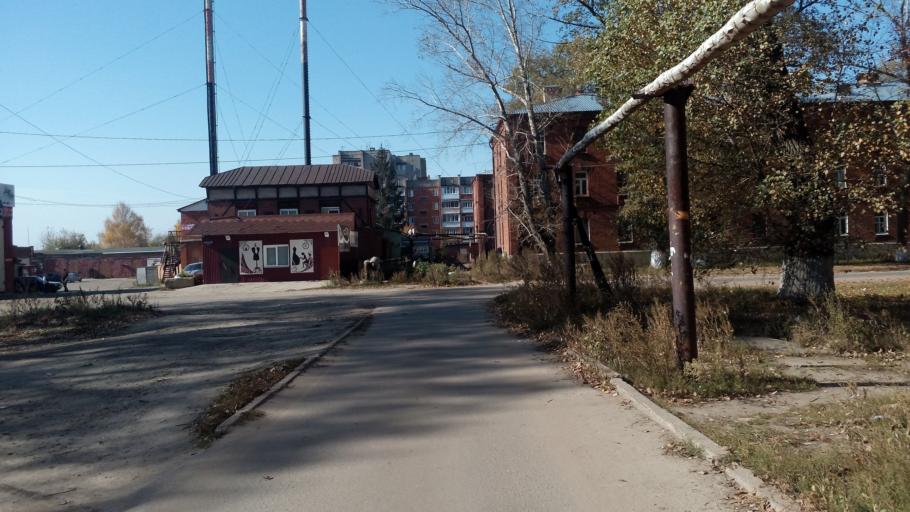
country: RU
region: Tambov
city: Kotovsk
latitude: 52.5838
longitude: 41.4982
